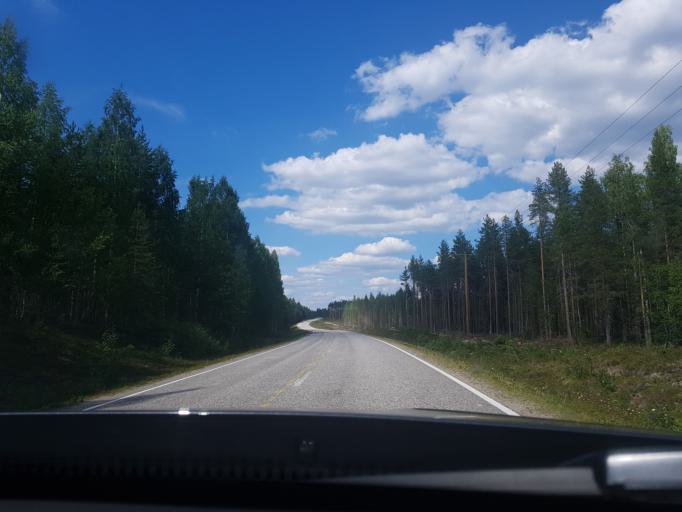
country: FI
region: Kainuu
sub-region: Kehys-Kainuu
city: Kuhmo
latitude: 64.2352
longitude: 29.8184
